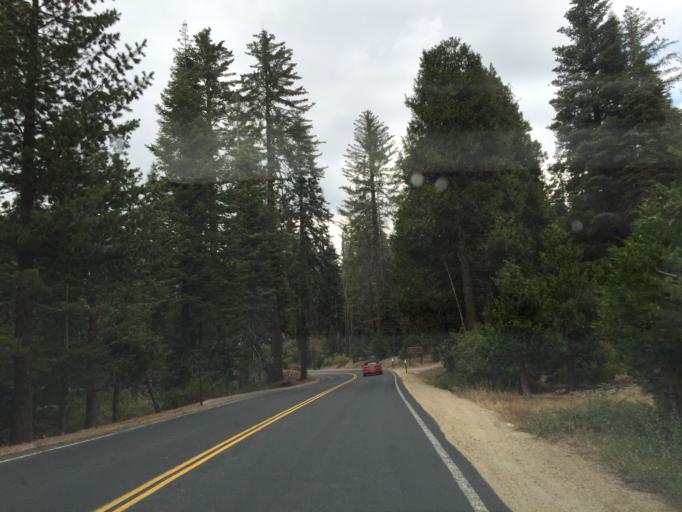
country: US
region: California
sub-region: Tulare County
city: Three Rivers
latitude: 36.7246
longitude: -118.9552
